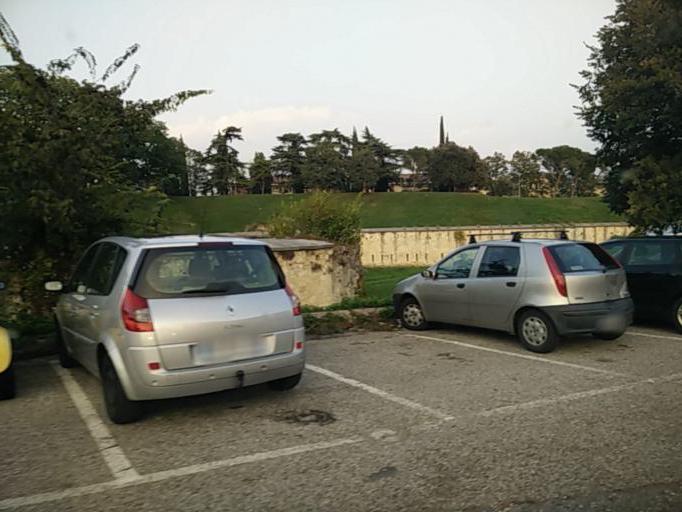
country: IT
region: Veneto
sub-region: Provincia di Verona
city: Verona
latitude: 45.4368
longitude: 10.9775
